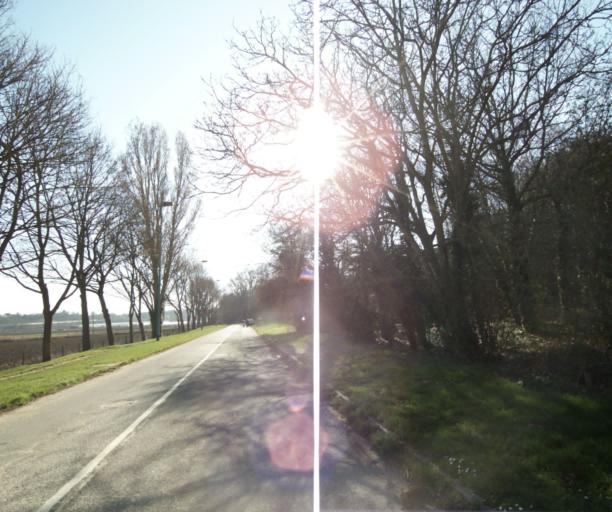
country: FR
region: Ile-de-France
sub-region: Departement du Val-d'Oise
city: Cergy
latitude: 49.0261
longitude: 2.0864
